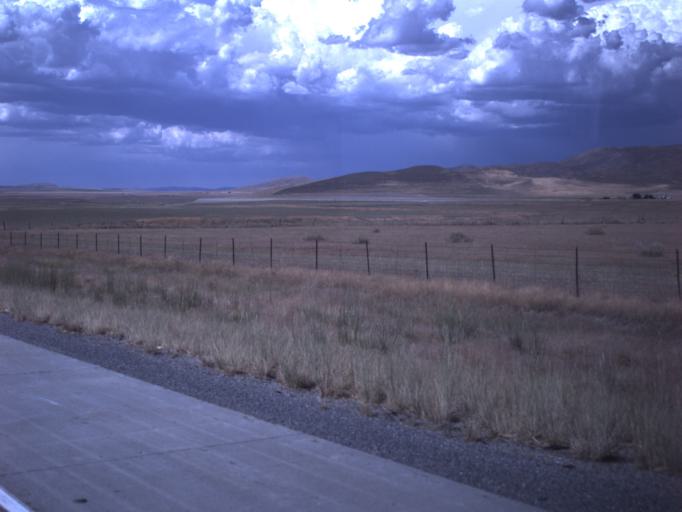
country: US
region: Utah
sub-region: Box Elder County
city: Garland
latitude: 41.8267
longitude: -112.4243
